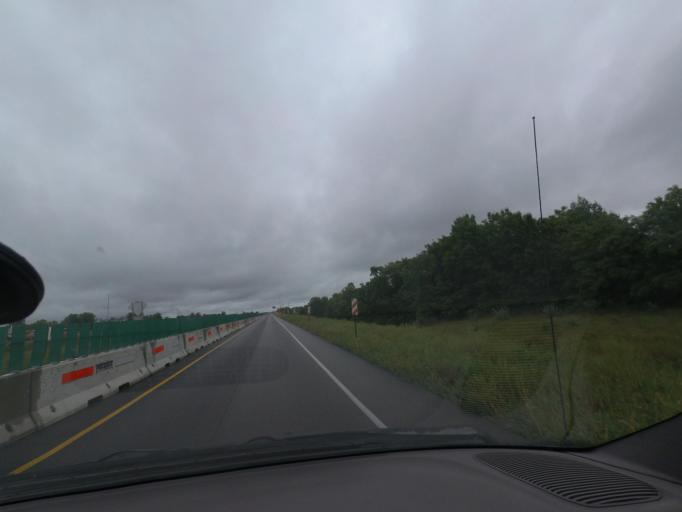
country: US
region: Illinois
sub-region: Piatt County
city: Cerro Gordo
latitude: 39.9868
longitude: -88.7872
